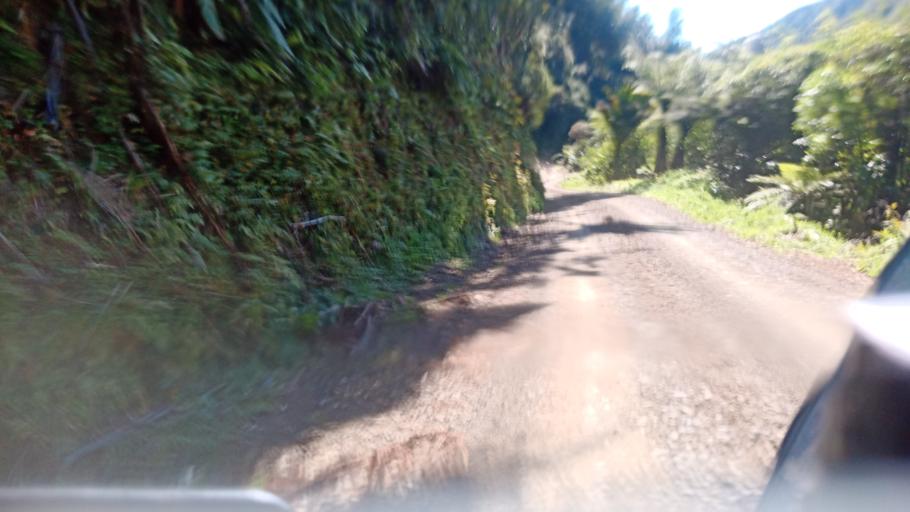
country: NZ
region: Bay of Plenty
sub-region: Opotiki District
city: Opotiki
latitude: -38.0741
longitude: 177.4733
